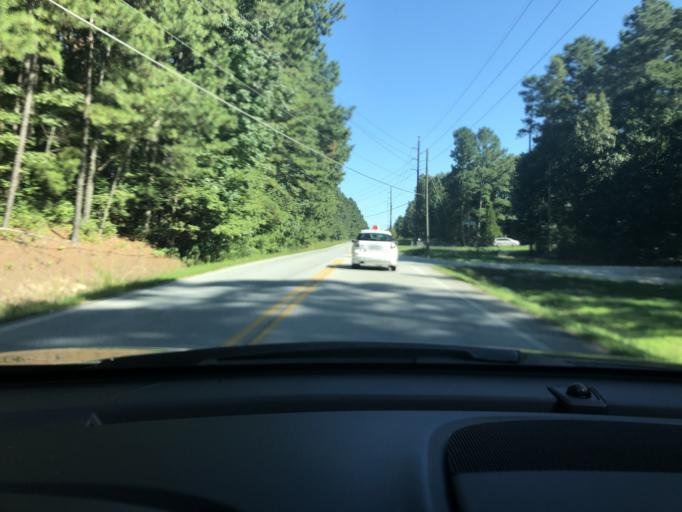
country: US
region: Georgia
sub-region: Gwinnett County
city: Grayson
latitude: 33.9168
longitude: -83.9383
